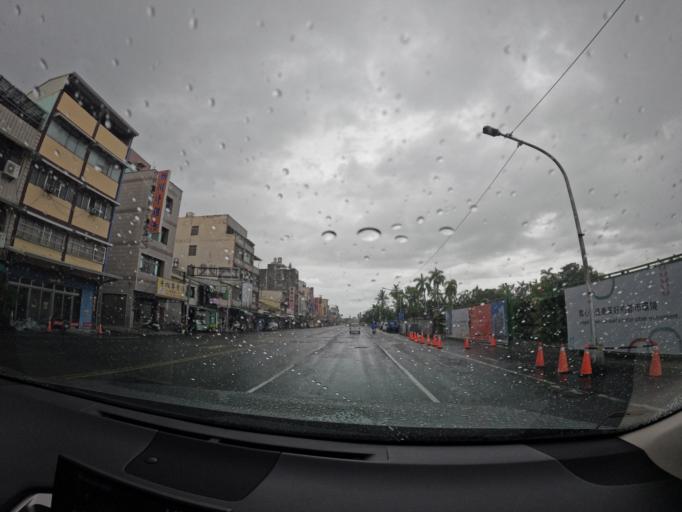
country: TW
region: Taiwan
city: Fengshan
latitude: 22.6429
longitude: 120.3644
